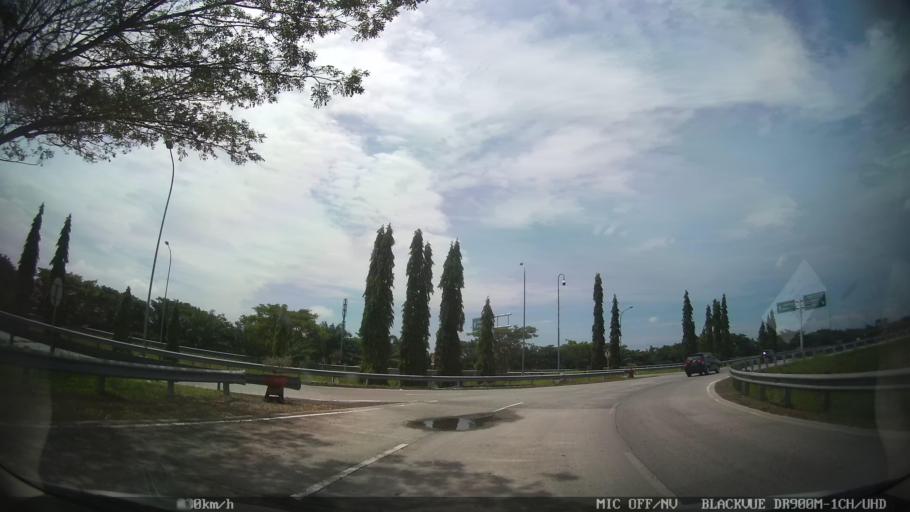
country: ID
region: North Sumatra
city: Percut
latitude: 3.6319
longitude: 98.8773
